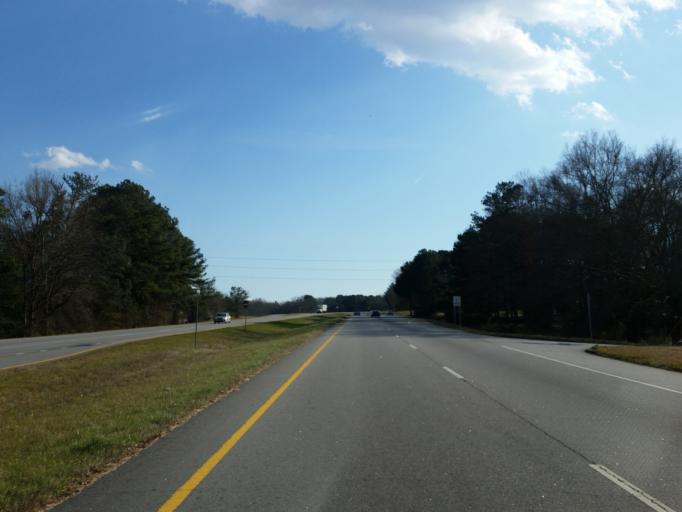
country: US
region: Georgia
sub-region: Lamar County
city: Barnesville
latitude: 33.0594
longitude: -84.1685
